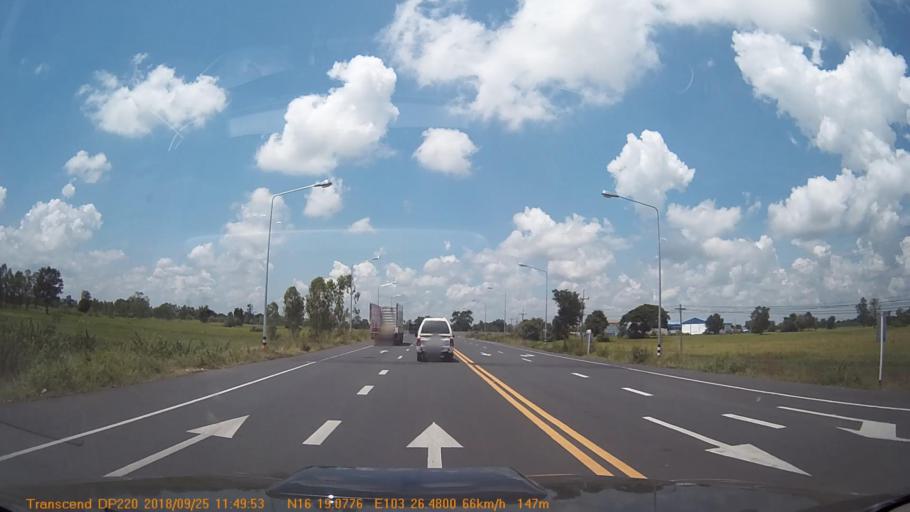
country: TH
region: Kalasin
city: Khong Chai
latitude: 16.3180
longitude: 103.4412
